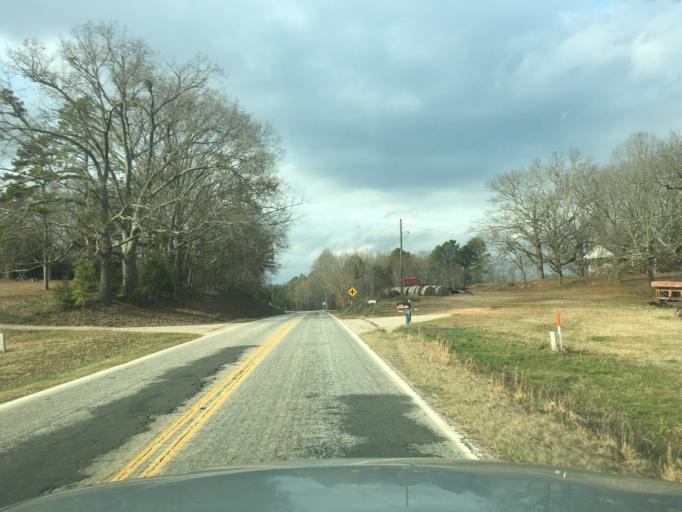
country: US
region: South Carolina
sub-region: Abbeville County
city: Due West
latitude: 34.2672
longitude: -82.4187
